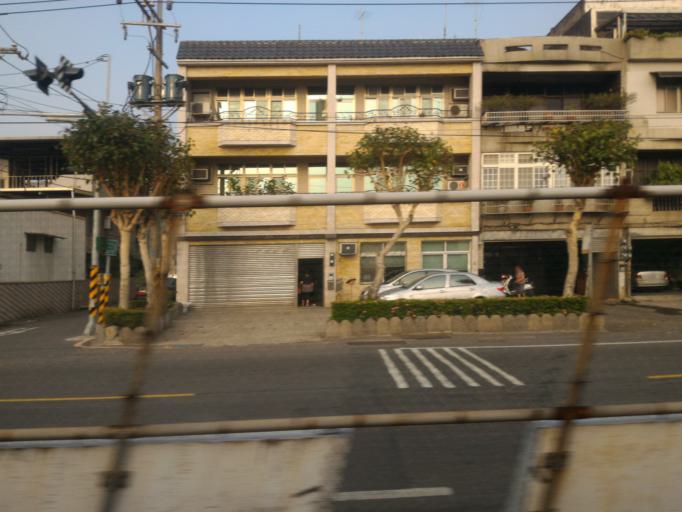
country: TW
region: Taiwan
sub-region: Taoyuan
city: Taoyuan
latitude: 24.9769
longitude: 121.3322
